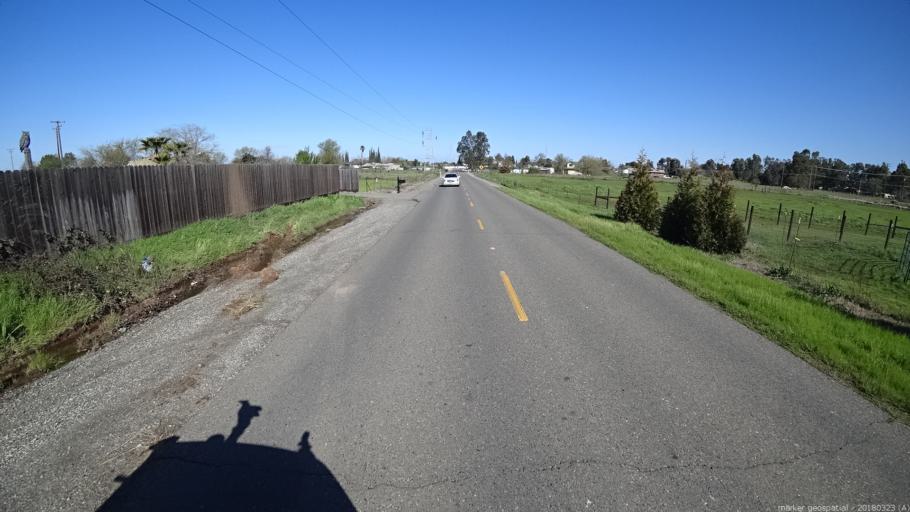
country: US
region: California
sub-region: Sacramento County
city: Rio Linda
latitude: 38.6894
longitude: -121.4721
